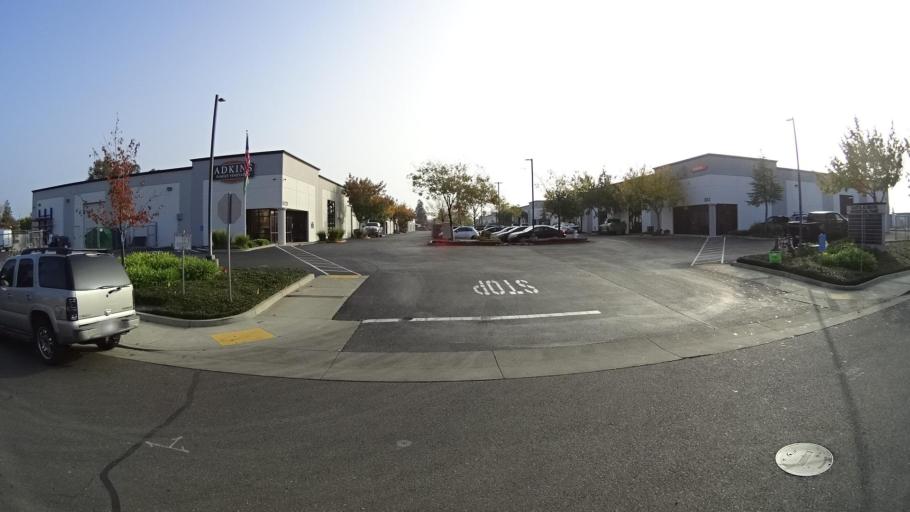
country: US
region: California
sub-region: Sacramento County
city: Elk Grove
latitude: 38.4041
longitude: -121.3594
